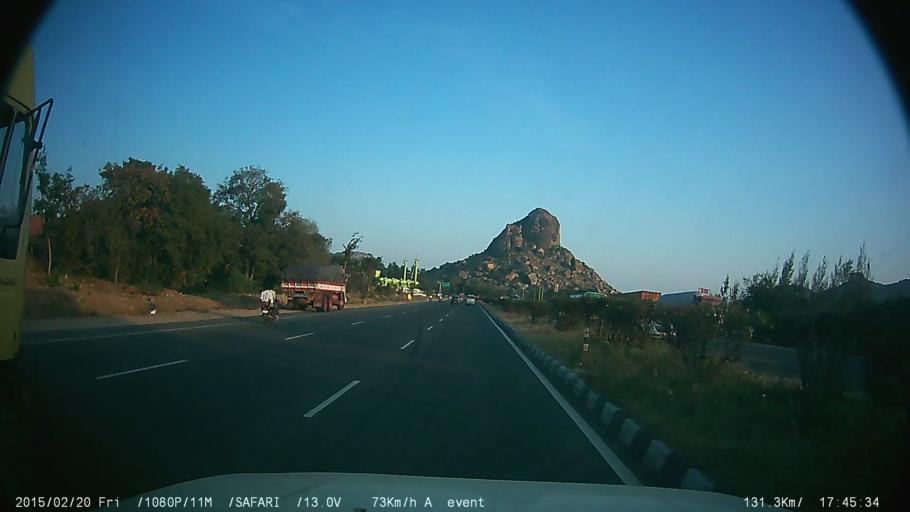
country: IN
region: Tamil Nadu
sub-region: Krishnagiri
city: Krishnagiri
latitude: 12.5550
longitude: 78.1877
